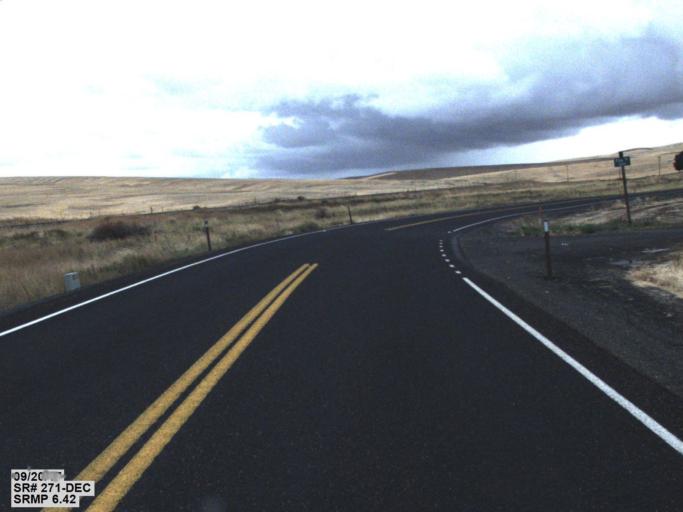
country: US
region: Washington
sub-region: Whitman County
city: Colfax
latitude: 47.1891
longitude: -117.3338
